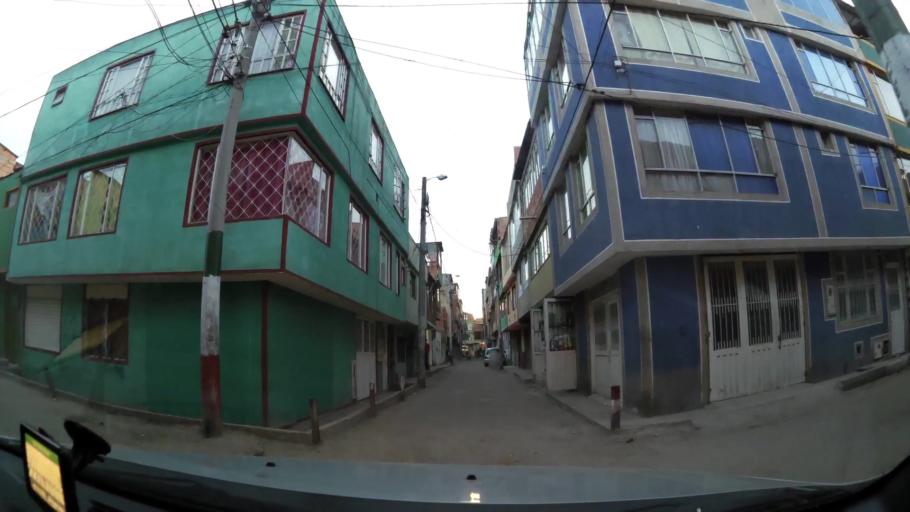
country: CO
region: Cundinamarca
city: Soacha
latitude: 4.6265
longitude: -74.1647
